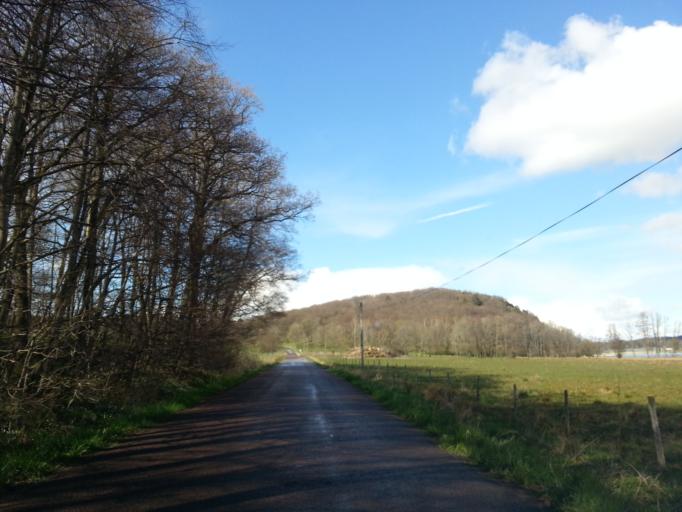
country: SE
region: Vaestra Goetaland
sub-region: Kungalvs Kommun
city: Diserod
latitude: 57.8847
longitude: 12.0285
